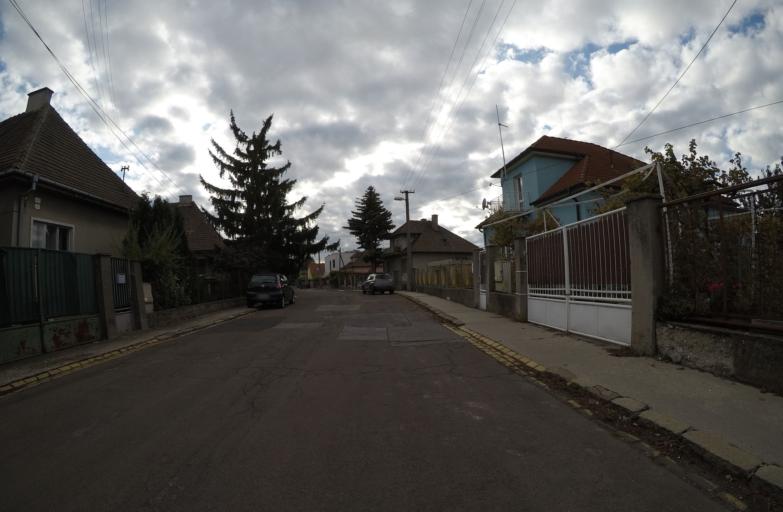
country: SK
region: Bratislavsky
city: Bratislava
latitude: 48.1669
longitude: 17.1694
